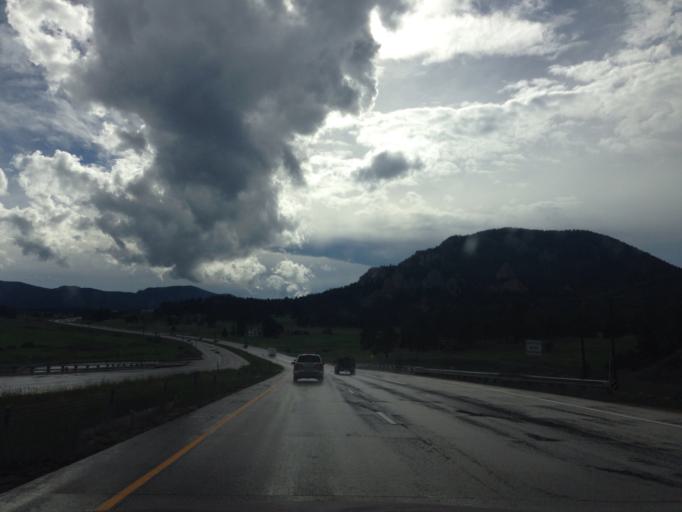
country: US
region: Colorado
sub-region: Jefferson County
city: Indian Hills
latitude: 39.5466
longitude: -105.2711
